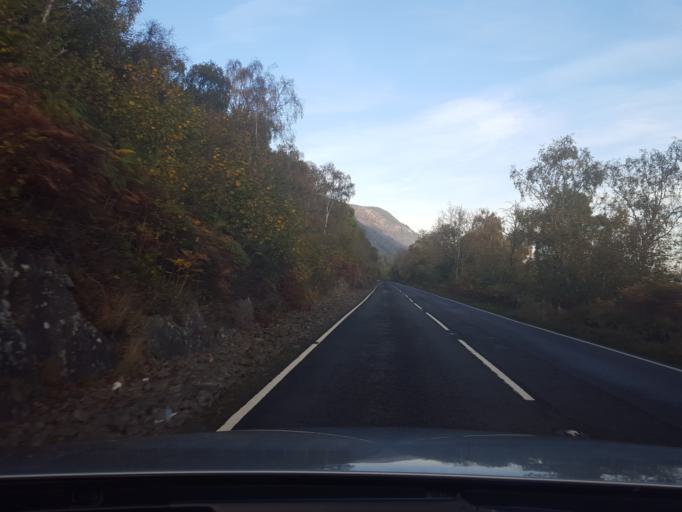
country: GB
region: Scotland
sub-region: Highland
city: Beauly
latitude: 57.3705
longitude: -4.3867
